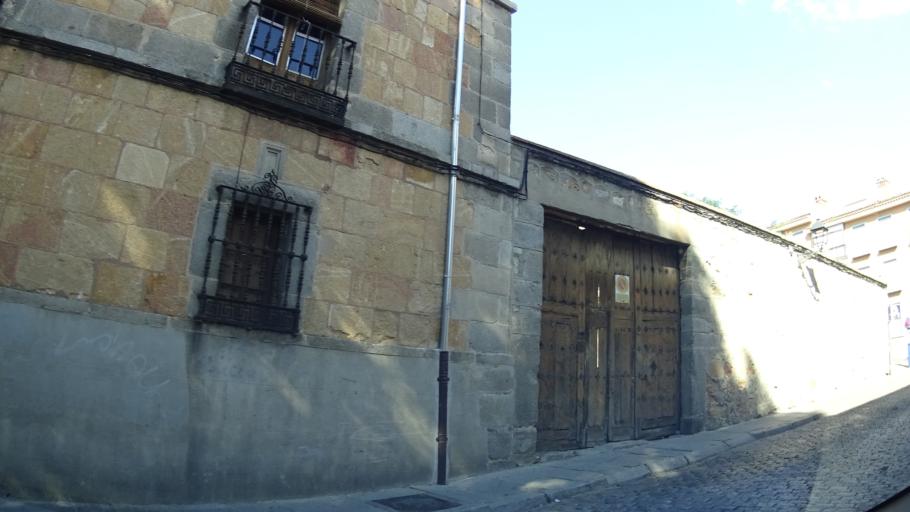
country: ES
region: Castille and Leon
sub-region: Provincia de Avila
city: Avila
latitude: 40.6558
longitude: -4.6954
